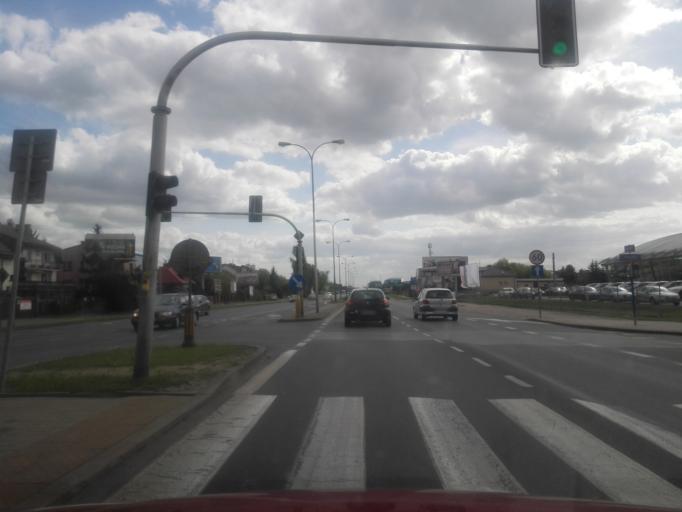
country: PL
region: Masovian Voivodeship
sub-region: Powiat wolominski
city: Zabki
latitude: 52.2911
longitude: 21.0787
